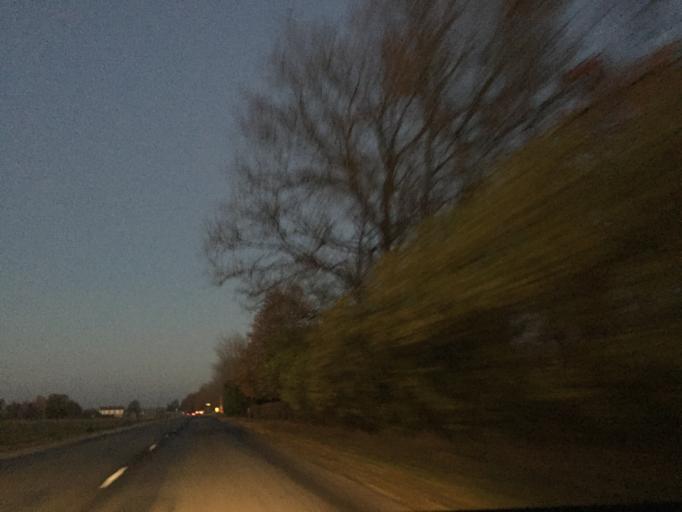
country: LV
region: Tervete
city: Zelmeni
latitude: 56.5177
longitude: 23.3233
